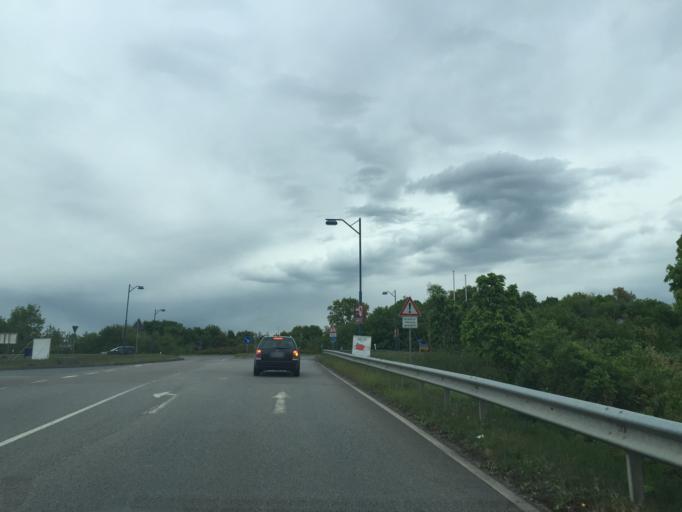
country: DE
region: Baden-Wuerttemberg
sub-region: Karlsruhe Region
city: Heddesheim
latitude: 49.5085
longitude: 8.6363
